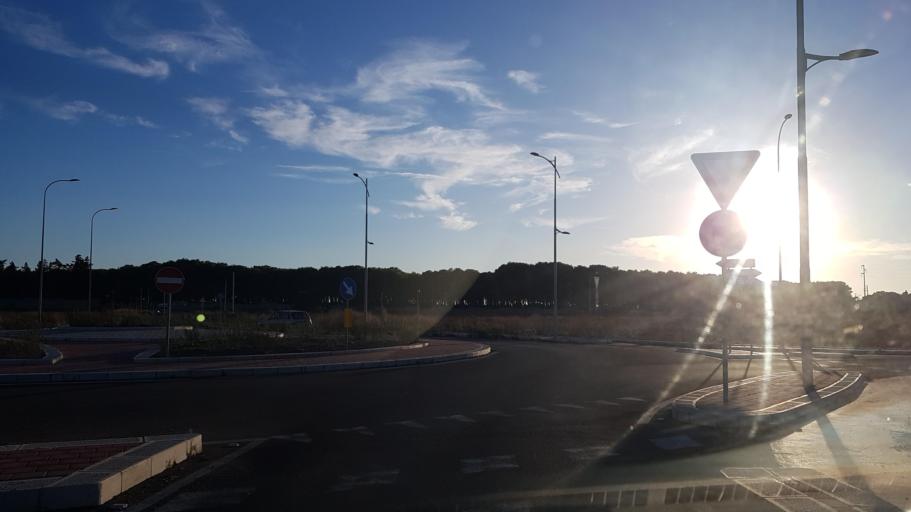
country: IT
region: Apulia
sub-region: Provincia di Lecce
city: Giorgilorio
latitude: 40.4124
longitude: 18.2025
